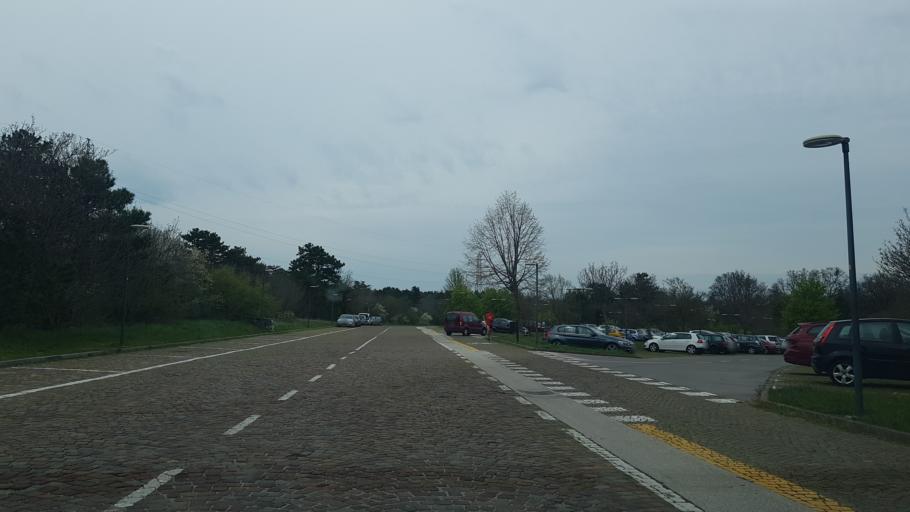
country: IT
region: Friuli Venezia Giulia
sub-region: Provincia di Trieste
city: Domio
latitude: 45.6445
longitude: 13.8466
